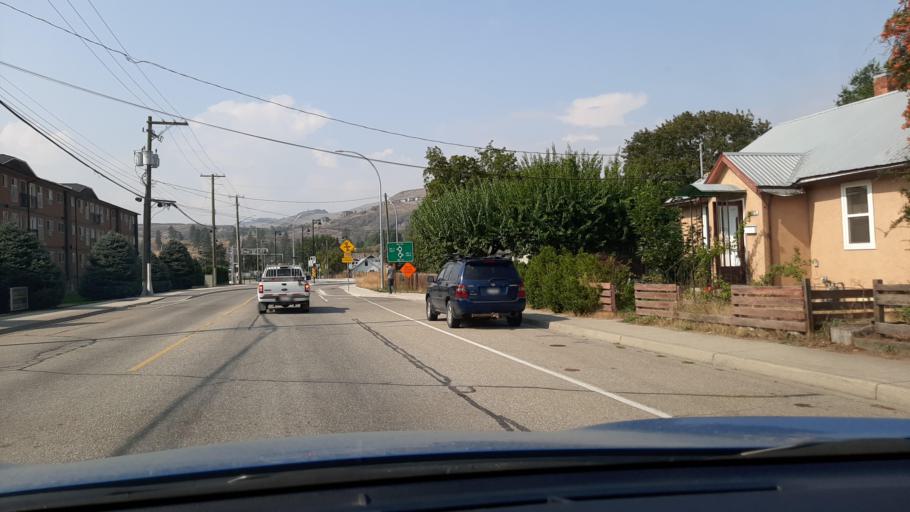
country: CA
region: British Columbia
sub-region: Regional District of North Okanagan
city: Vernon
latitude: 50.2702
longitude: -119.2692
